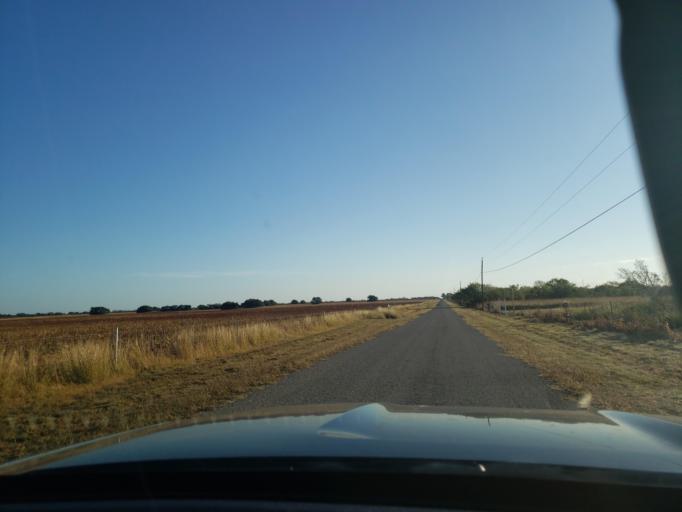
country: US
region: Texas
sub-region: Bee County
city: Beeville
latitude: 28.4264
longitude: -97.6996
